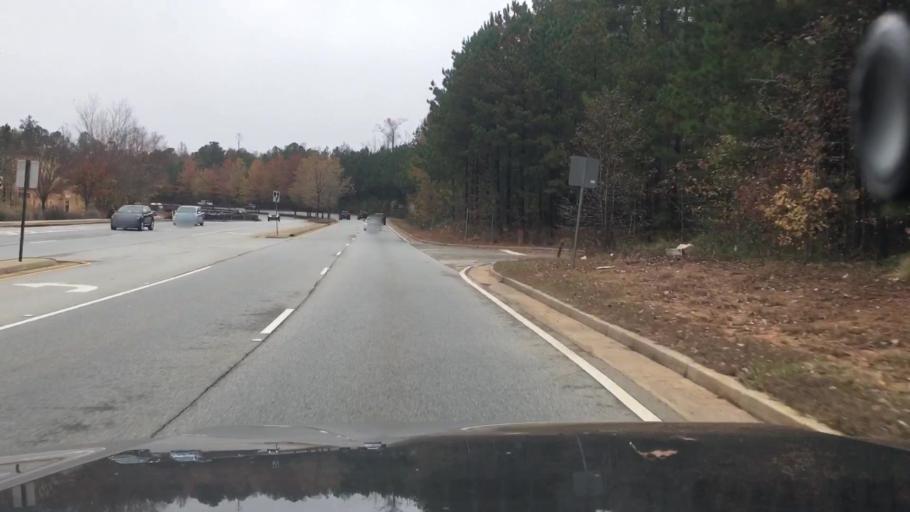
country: US
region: Georgia
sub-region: Coweta County
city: East Newnan
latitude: 33.3785
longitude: -84.7607
